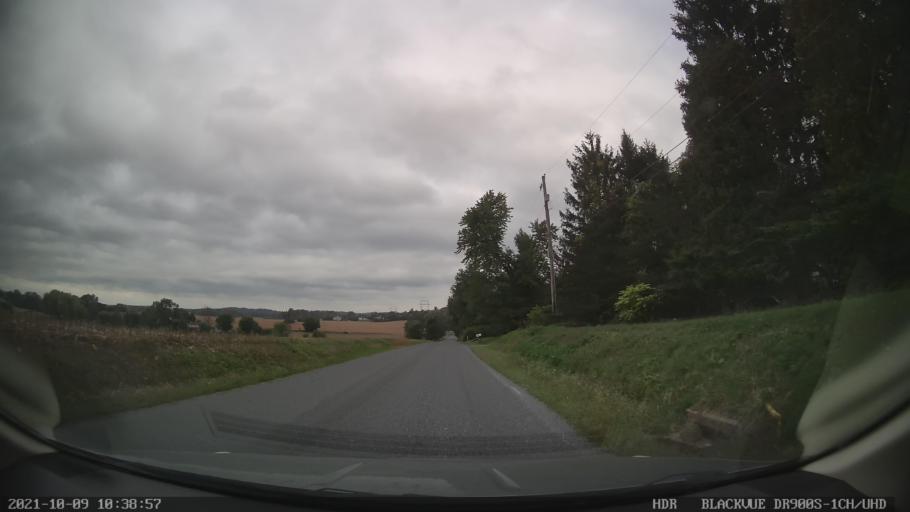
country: US
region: Pennsylvania
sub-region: Lehigh County
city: Breinigsville
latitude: 40.5144
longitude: -75.6309
